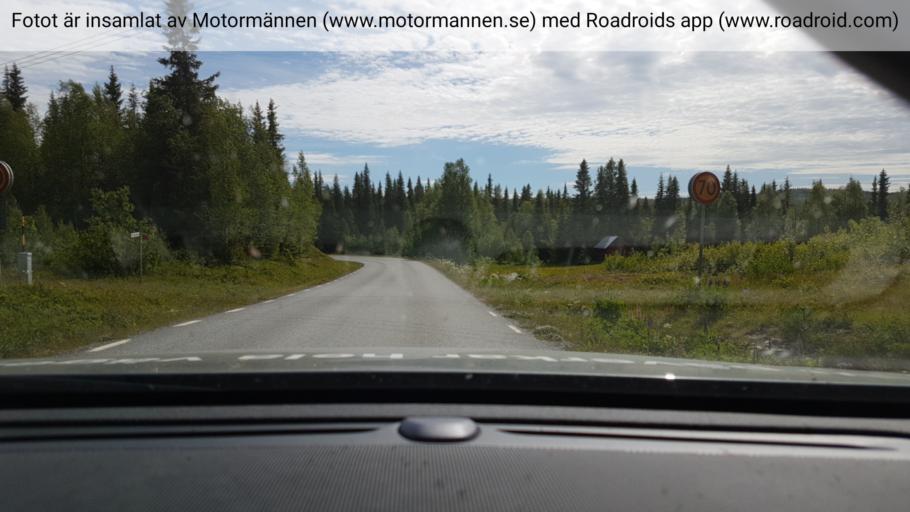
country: SE
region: Vaesterbotten
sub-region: Vilhelmina Kommun
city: Sjoberg
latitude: 65.2319
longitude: 16.0009
